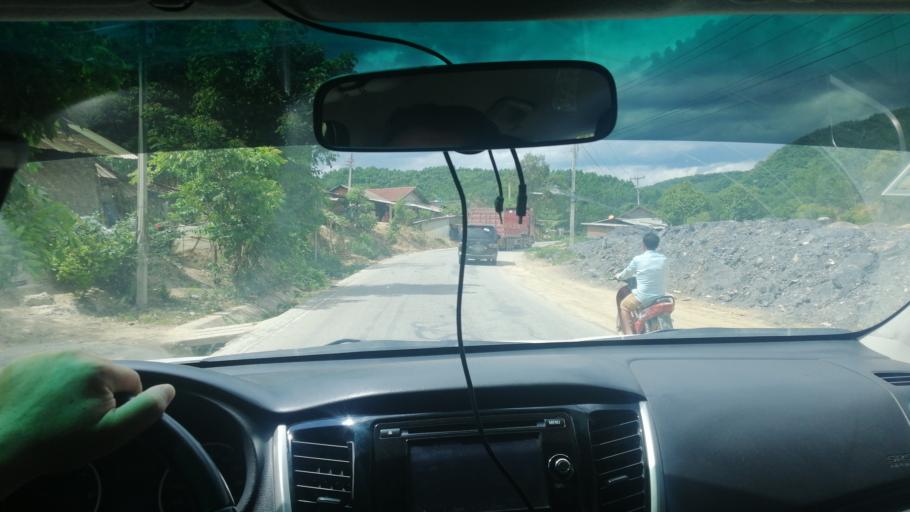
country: LA
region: Loungnamtha
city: Louang Namtha
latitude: 21.0394
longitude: 101.6499
